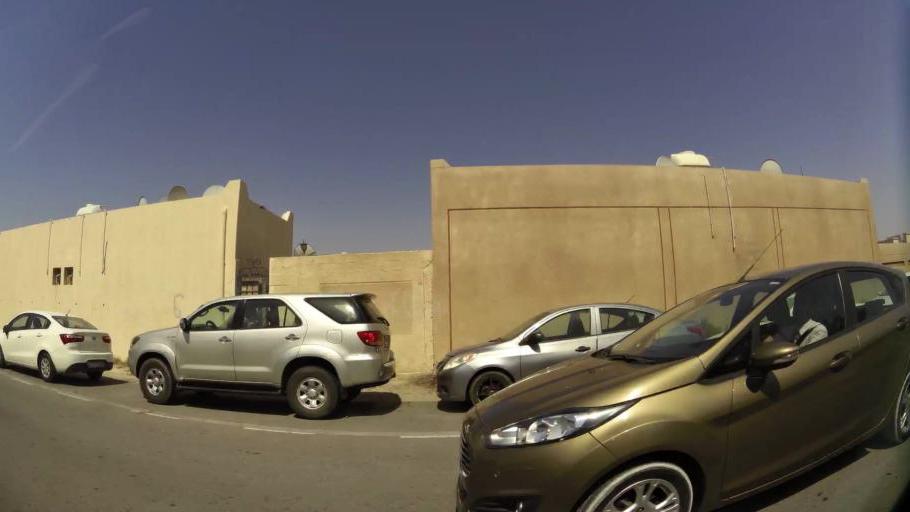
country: AE
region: Ash Shariqah
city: Sharjah
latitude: 25.2699
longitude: 55.3607
